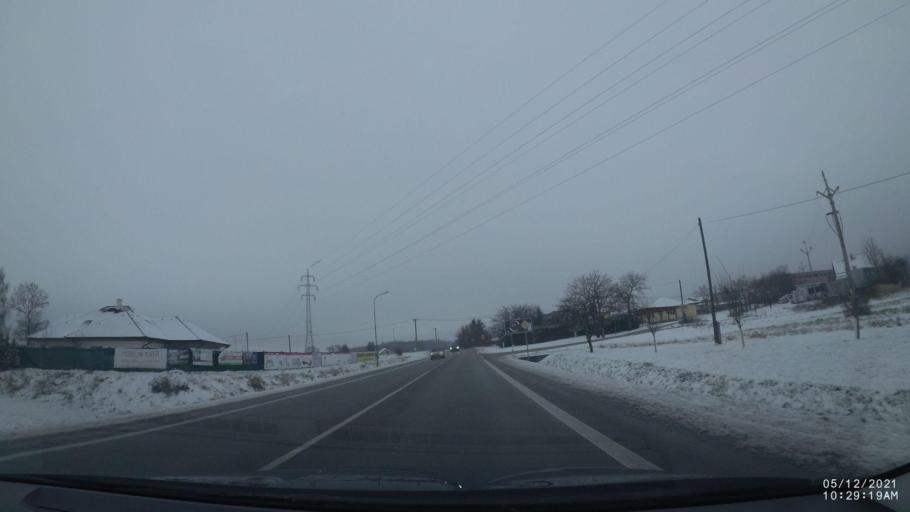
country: CZ
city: Vamberk
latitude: 50.1318
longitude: 16.2856
